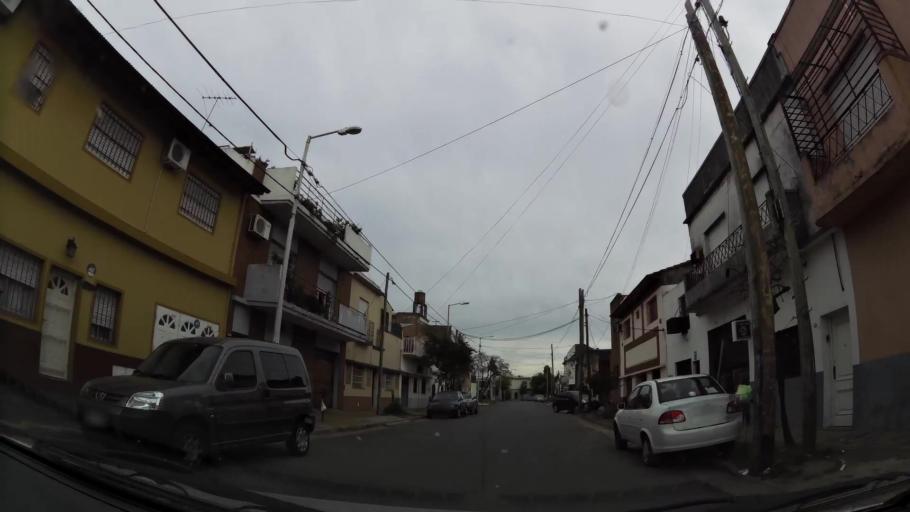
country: AR
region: Buenos Aires
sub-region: Partido de Avellaneda
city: Avellaneda
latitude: -34.6751
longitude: -58.3461
